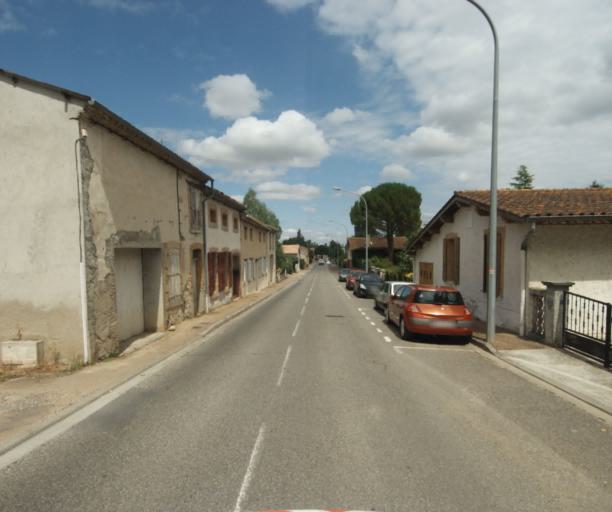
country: FR
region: Midi-Pyrenees
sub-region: Departement de la Haute-Garonne
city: Revel
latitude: 43.4515
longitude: 1.9996
